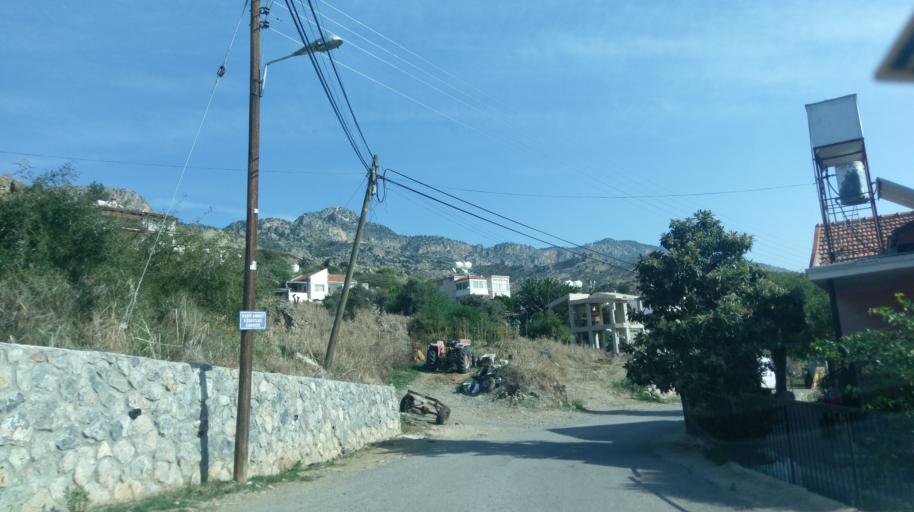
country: CY
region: Keryneia
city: Kyrenia
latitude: 35.2711
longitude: 33.3915
